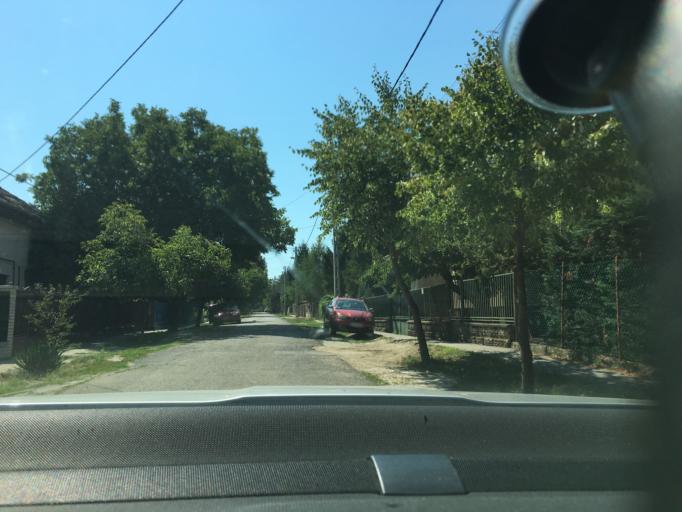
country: HU
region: Budapest
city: Budapest XVI. keruelet
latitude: 47.5070
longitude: 19.1908
